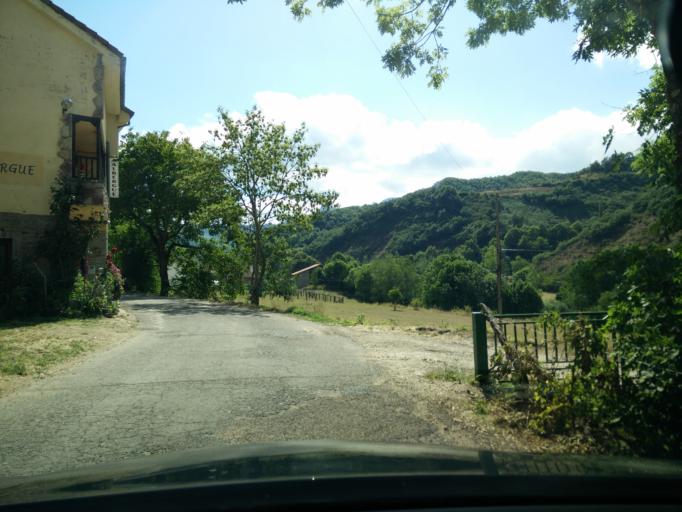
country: ES
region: Castille and Leon
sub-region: Provincia de Leon
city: Posada de Valdeon
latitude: 43.1560
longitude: -4.9145
